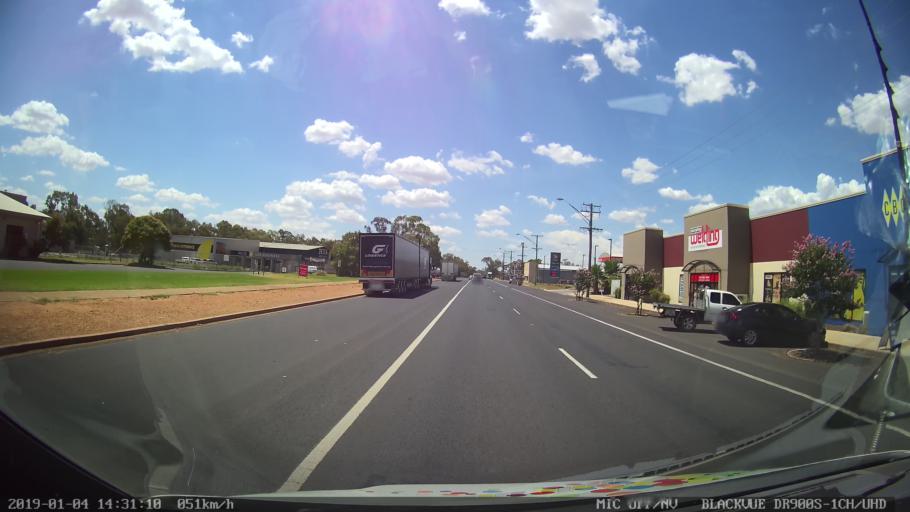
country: AU
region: New South Wales
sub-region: Dubbo Municipality
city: Dubbo
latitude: -32.2335
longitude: 148.6113
